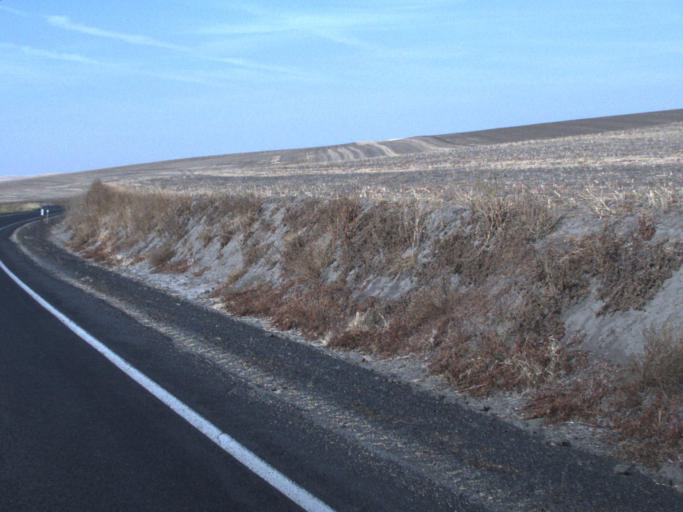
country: US
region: Idaho
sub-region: Benewah County
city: Plummer
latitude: 47.1815
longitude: -117.1736
